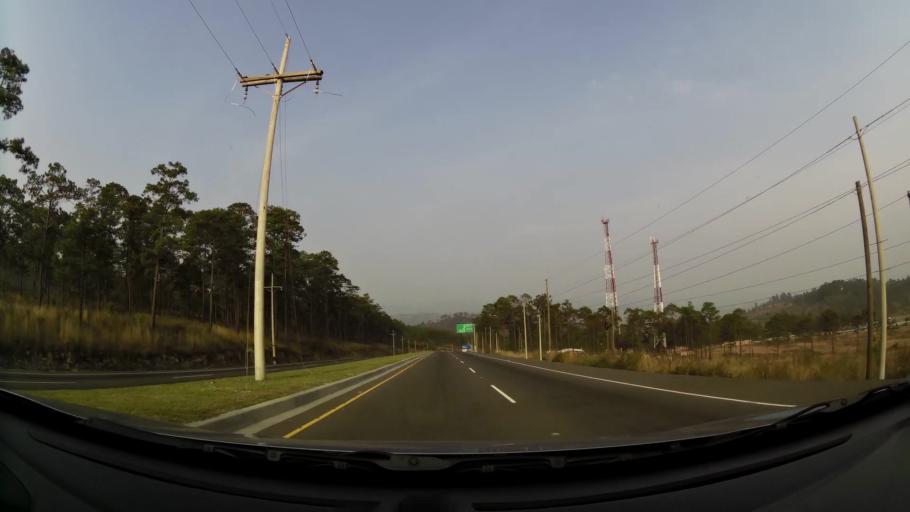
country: HN
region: Francisco Morazan
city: Tamara
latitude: 14.1687
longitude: -87.3073
